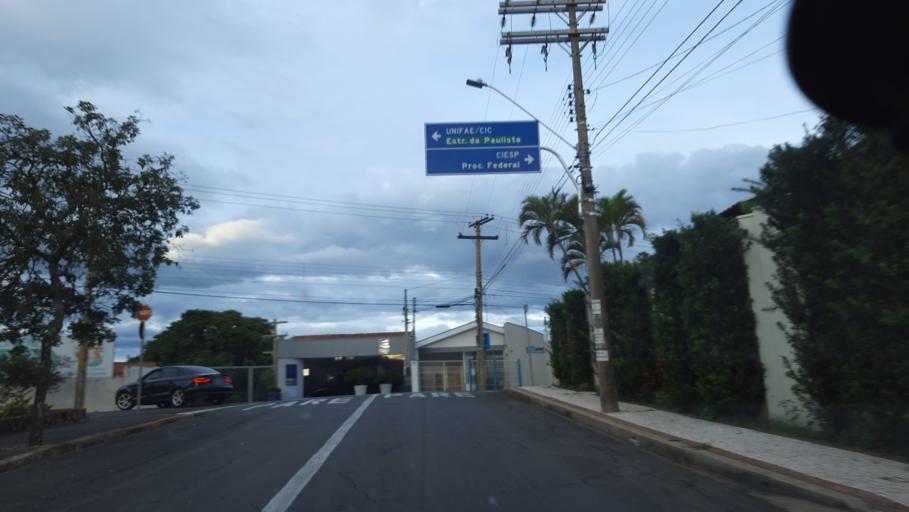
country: BR
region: Sao Paulo
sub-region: Sao Joao Da Boa Vista
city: Sao Joao da Boa Vista
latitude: -21.9658
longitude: -46.7915
